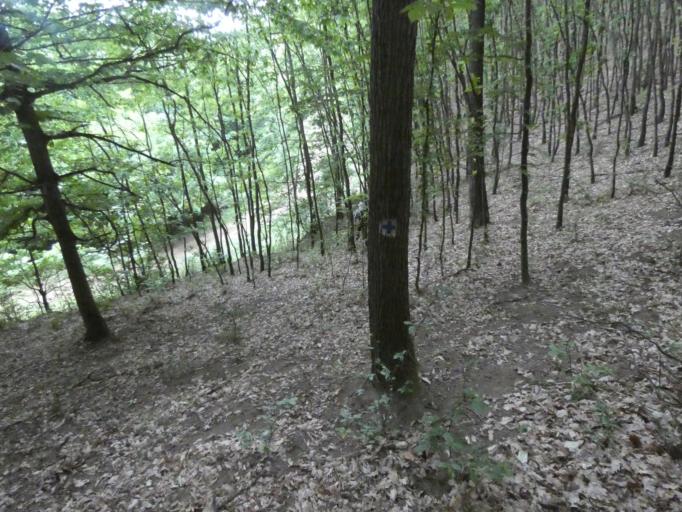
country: HU
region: Heves
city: Petervasara
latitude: 48.1192
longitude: 20.1051
